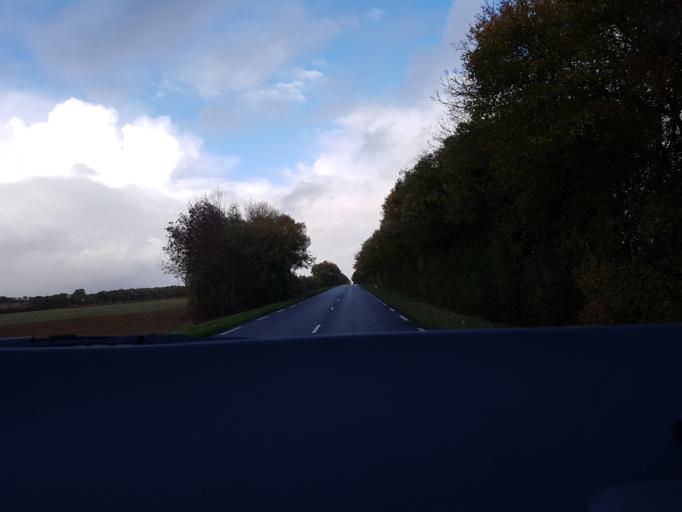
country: FR
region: Poitou-Charentes
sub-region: Departement de la Charente-Maritime
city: Aulnay
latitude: 46.0695
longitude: -0.3123
